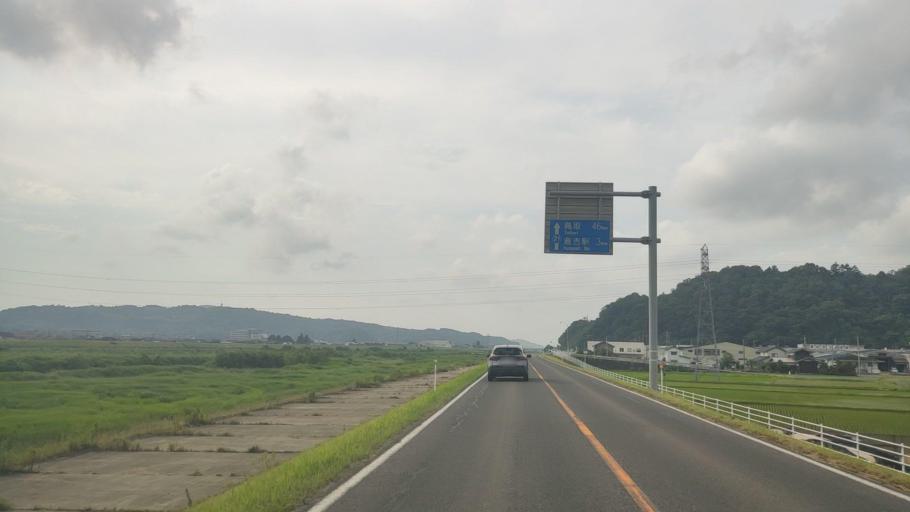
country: JP
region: Tottori
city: Kurayoshi
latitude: 35.4256
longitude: 133.8510
